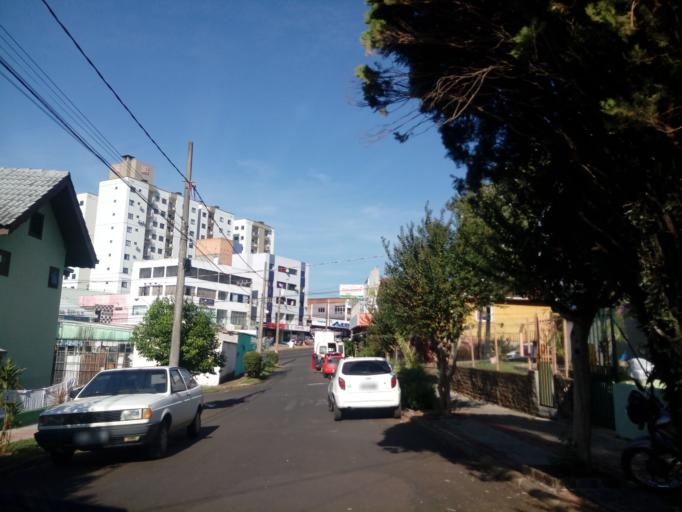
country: BR
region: Santa Catarina
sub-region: Chapeco
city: Chapeco
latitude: -27.0953
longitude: -52.6287
